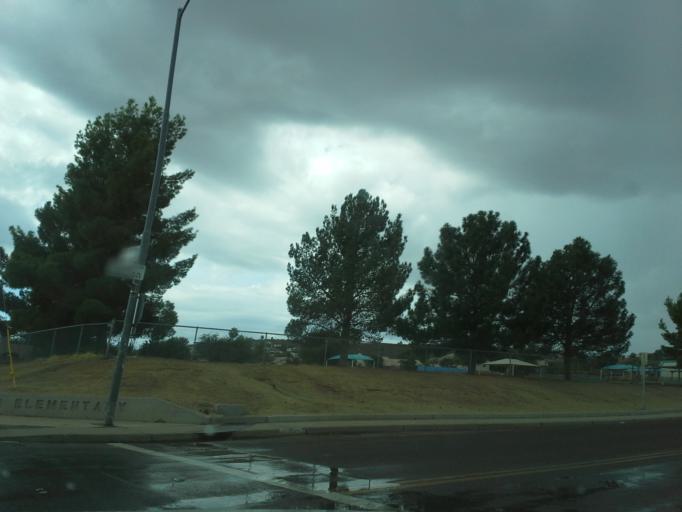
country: US
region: Arizona
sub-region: Maricopa County
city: Paradise Valley
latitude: 33.6114
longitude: -112.0394
